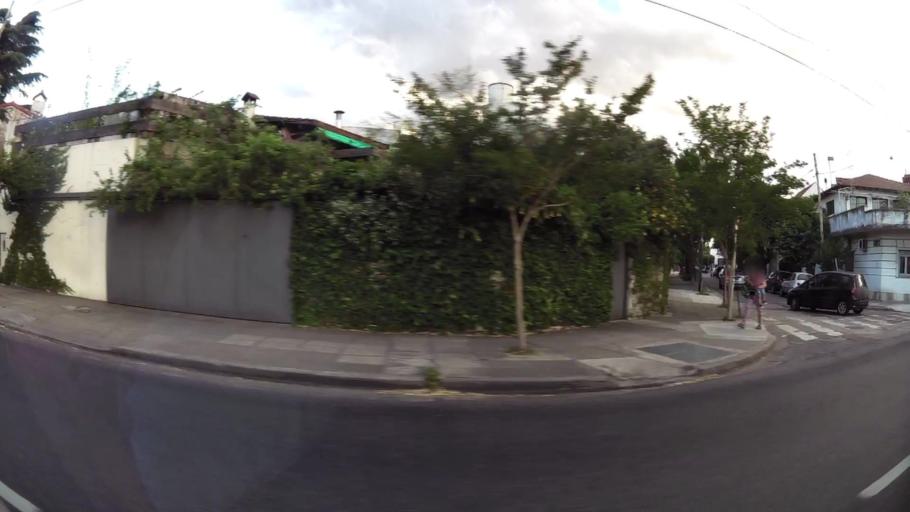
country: AR
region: Buenos Aires
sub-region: Partido de General San Martin
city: General San Martin
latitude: -34.5853
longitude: -58.5163
